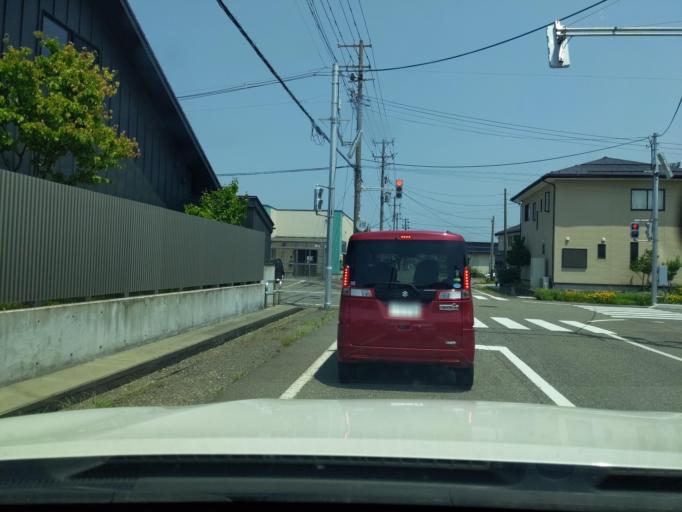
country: JP
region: Niigata
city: Kashiwazaki
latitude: 37.3649
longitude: 138.5848
